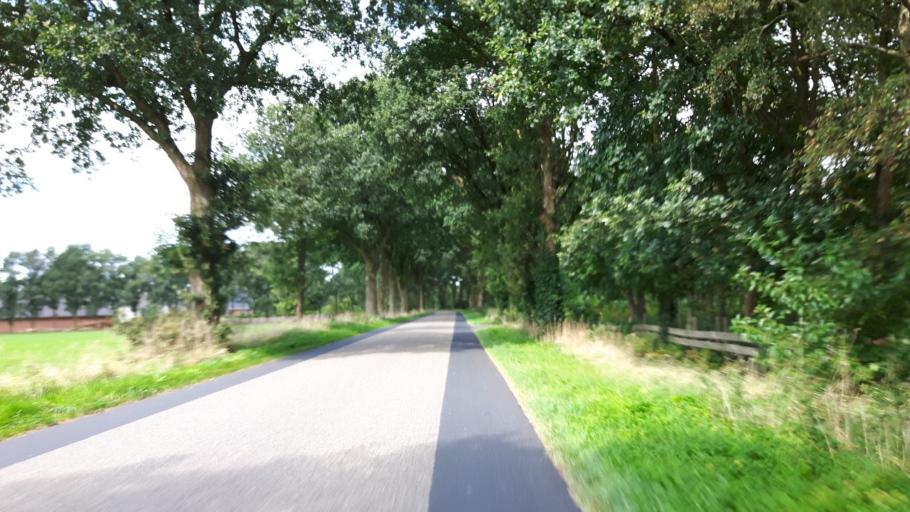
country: NL
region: Groningen
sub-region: Gemeente Leek
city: Leek
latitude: 53.0863
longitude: 6.3179
